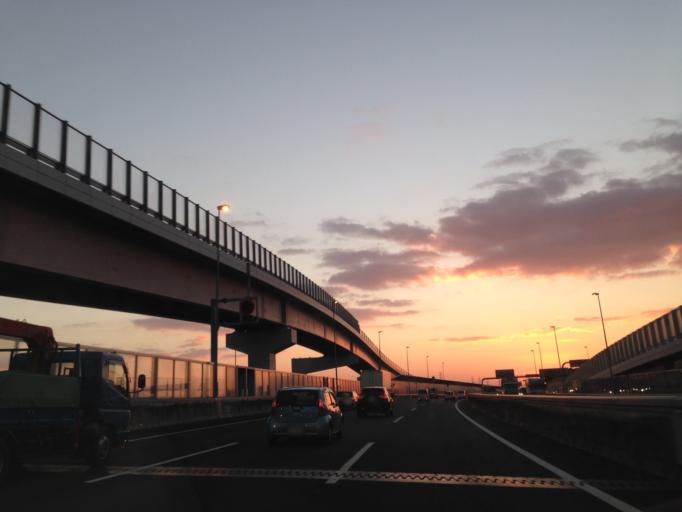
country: JP
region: Aichi
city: Obu
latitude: 35.0482
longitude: 136.9461
